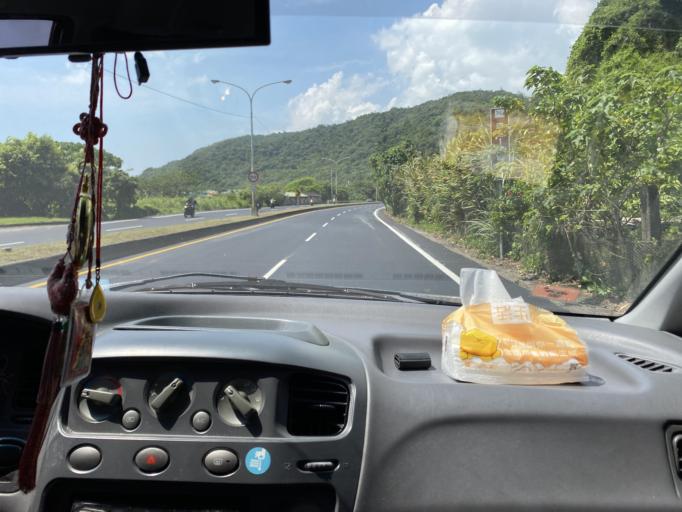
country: TW
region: Taiwan
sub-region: Yilan
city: Yilan
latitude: 24.8927
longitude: 121.8545
